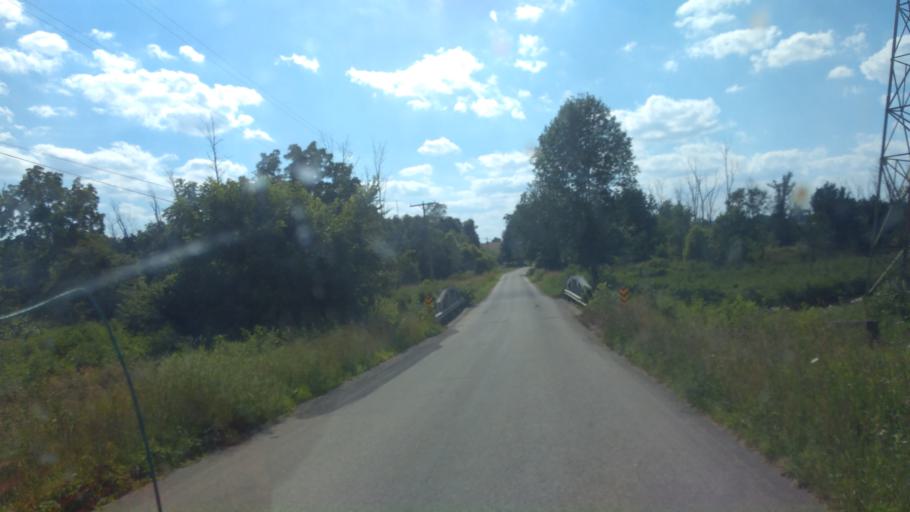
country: US
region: Ohio
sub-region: Stark County
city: Brewster
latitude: 40.7298
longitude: -81.6461
